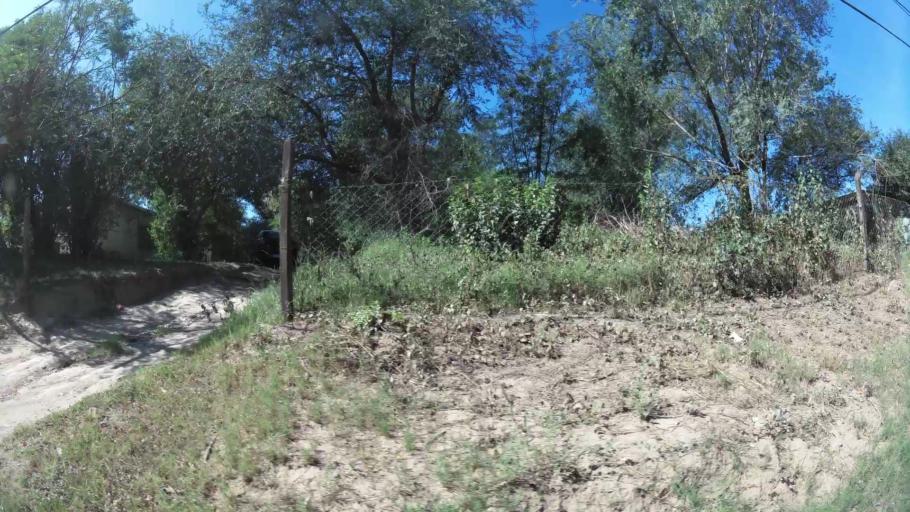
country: AR
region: Cordoba
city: Mendiolaza
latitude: -31.2697
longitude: -64.2985
